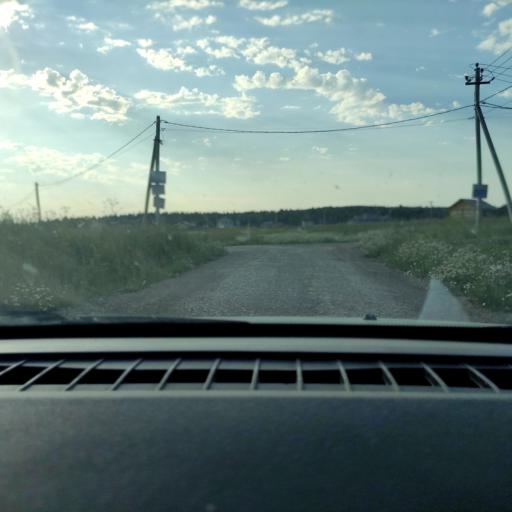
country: RU
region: Perm
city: Ferma
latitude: 57.9507
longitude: 56.3561
